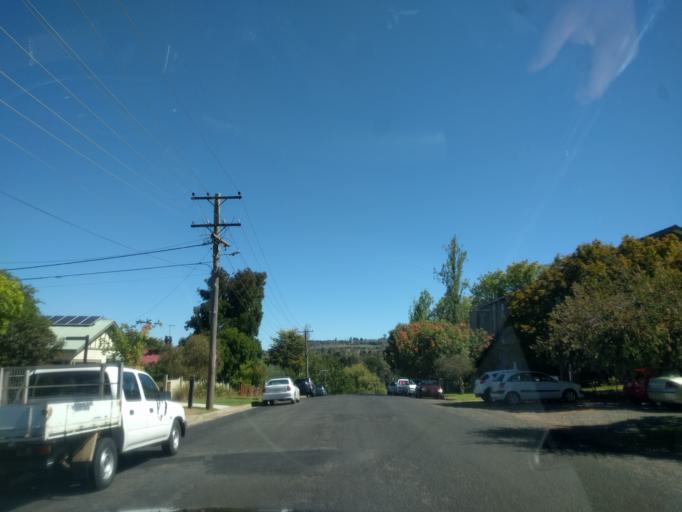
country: AU
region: New South Wales
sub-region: Armidale Dumaresq
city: Armidale
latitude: -30.5234
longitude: 151.6636
